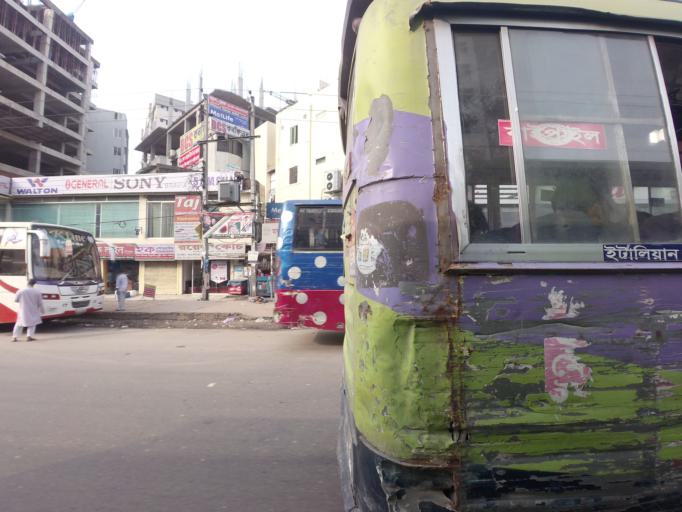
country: BD
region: Dhaka
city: Azimpur
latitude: 23.7753
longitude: 90.3648
